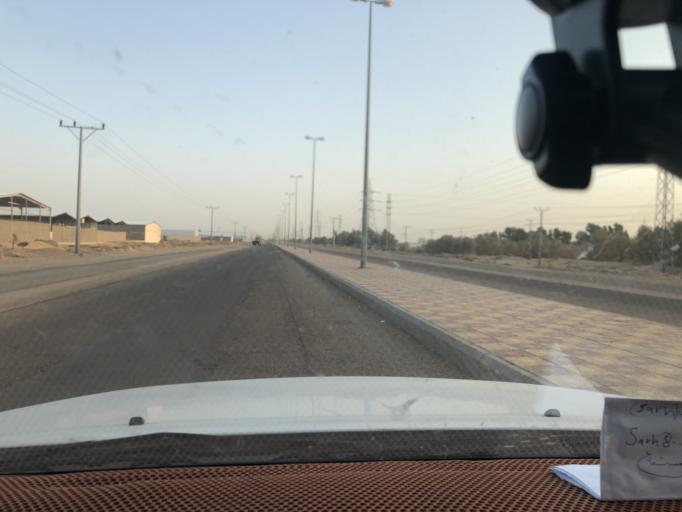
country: SA
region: Ar Riyad
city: As Sulayyil
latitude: 20.4067
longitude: 44.8715
